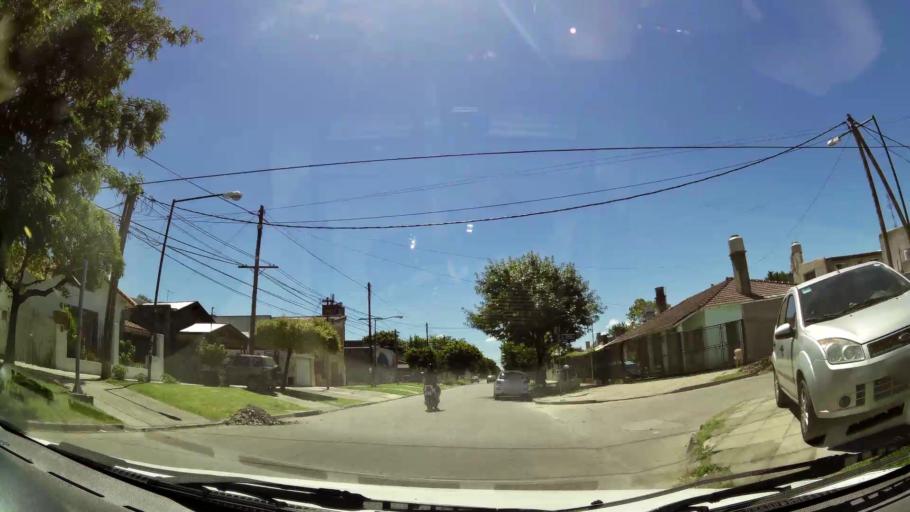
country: AR
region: Buenos Aires
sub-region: Partido de General San Martin
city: General San Martin
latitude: -34.5174
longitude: -58.5575
